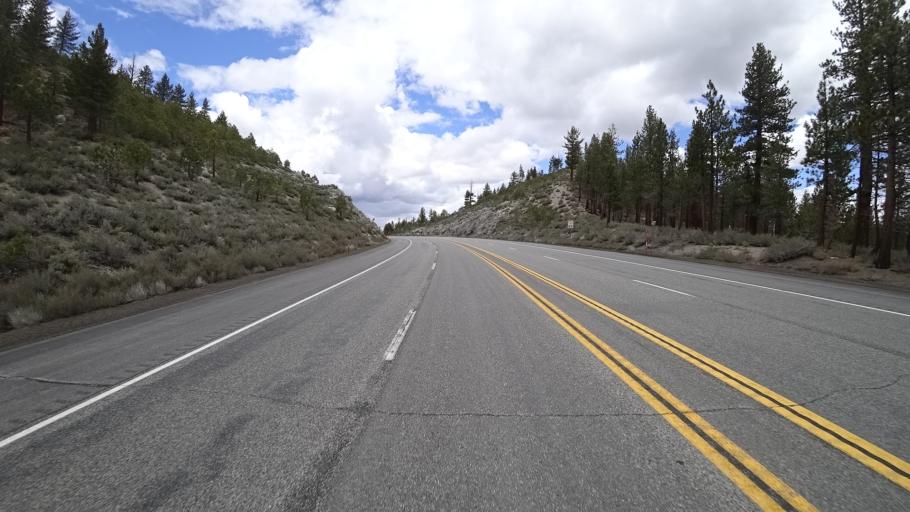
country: US
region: California
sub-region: Mono County
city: Mammoth Lakes
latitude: 37.8027
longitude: -119.0410
